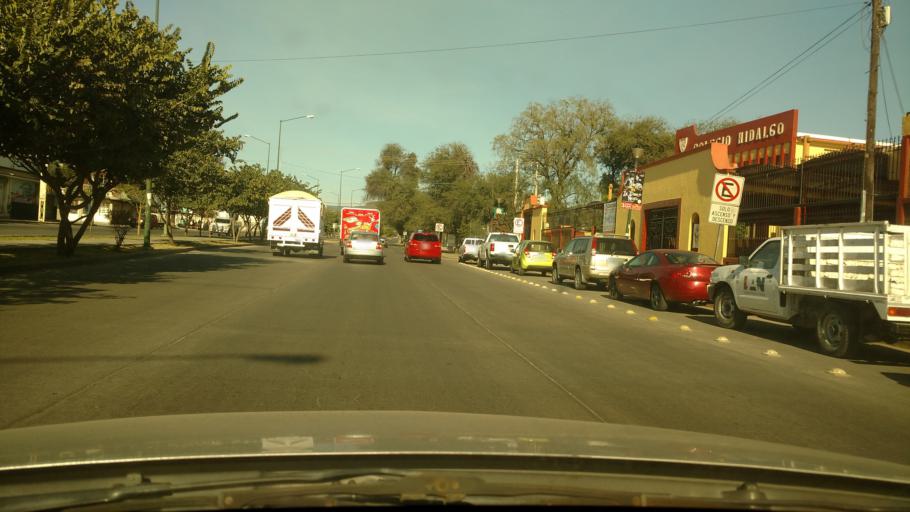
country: MX
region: Guanajuato
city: Leon
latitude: 21.1667
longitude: -101.6617
